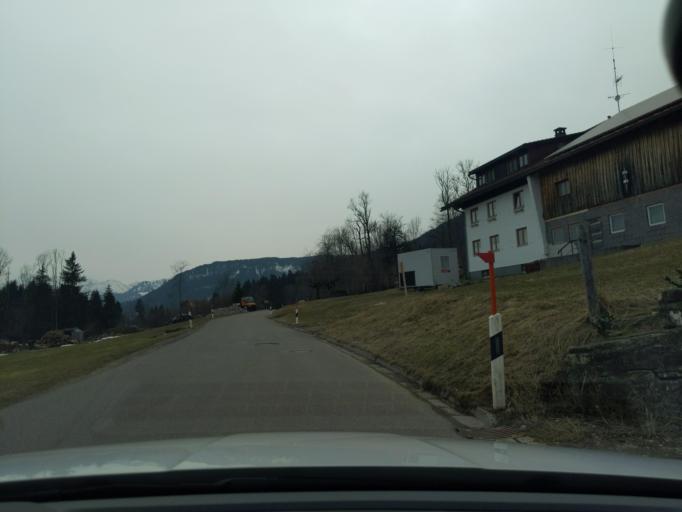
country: DE
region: Bavaria
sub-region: Swabia
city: Bolsterlang
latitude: 47.4712
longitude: 10.2308
